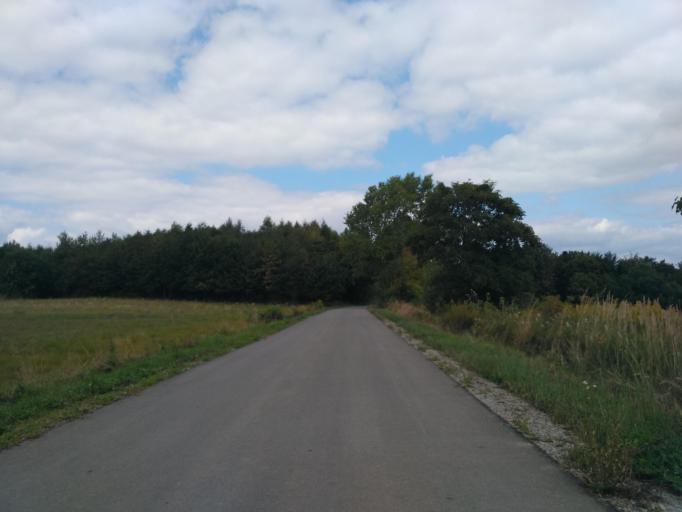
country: PL
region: Subcarpathian Voivodeship
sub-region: Powiat rzeszowski
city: Dynow
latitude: 49.7756
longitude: 22.2792
